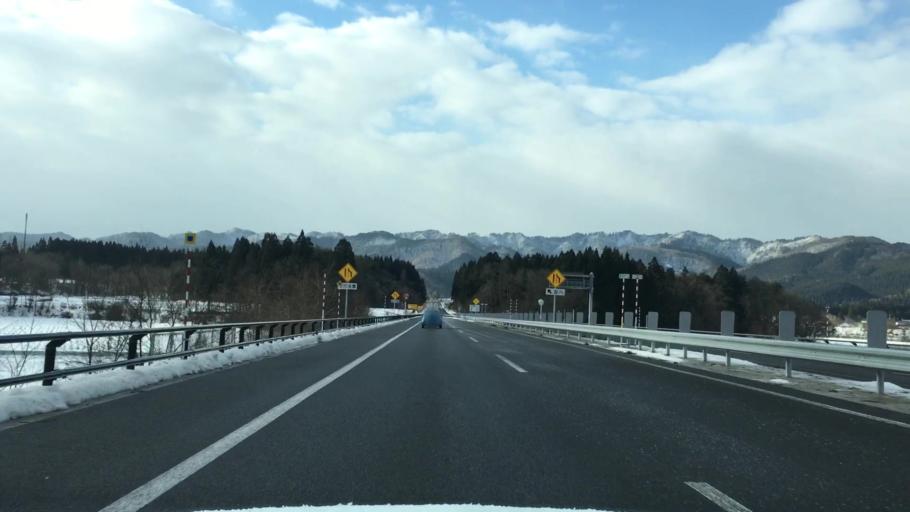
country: JP
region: Akita
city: Odate
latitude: 40.2469
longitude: 140.5126
